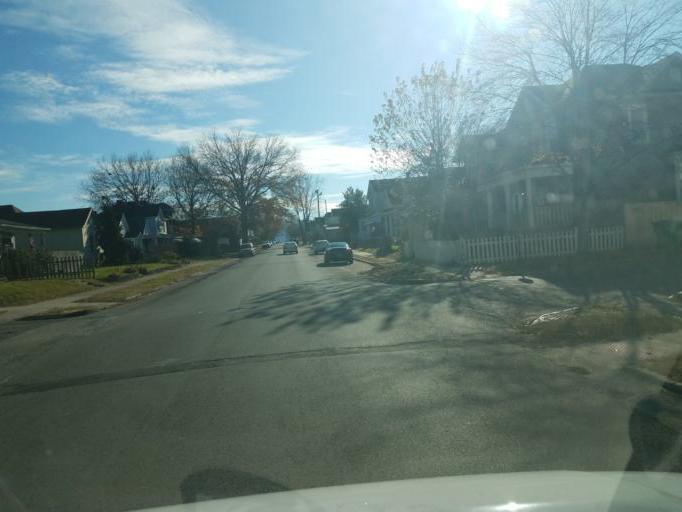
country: US
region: Ohio
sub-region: Scioto County
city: Portsmouth
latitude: 38.7453
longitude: -82.9751
